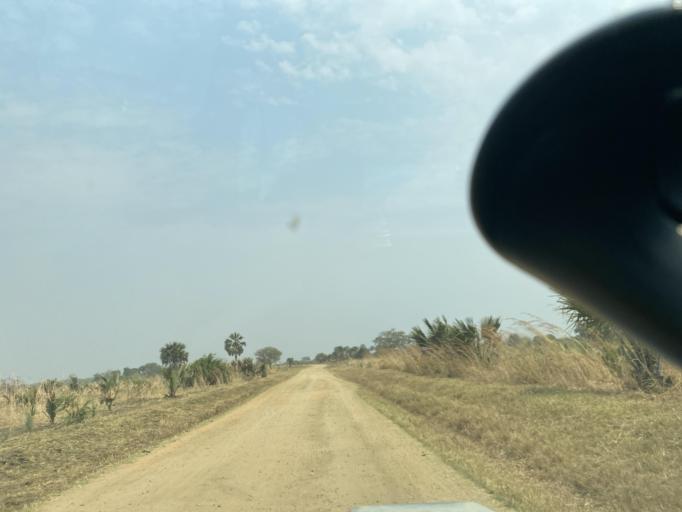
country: ZM
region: Lusaka
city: Kafue
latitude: -15.6501
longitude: 28.0487
